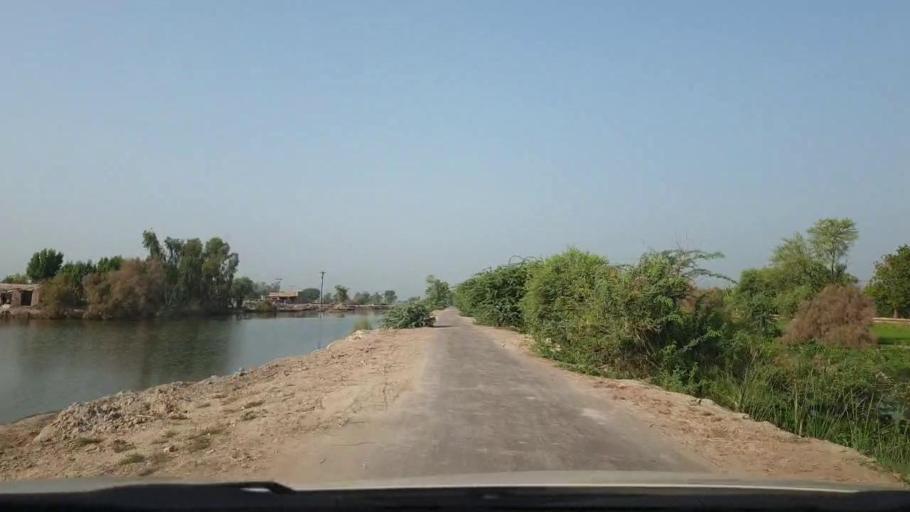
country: PK
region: Sindh
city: Larkana
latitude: 27.4897
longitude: 68.1658
